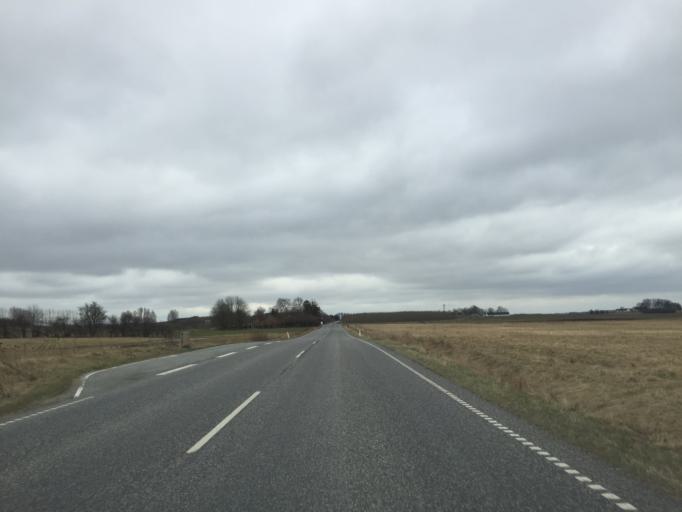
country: DK
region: Capital Region
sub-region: Allerod Kommune
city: Lynge
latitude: 55.8782
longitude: 12.2731
